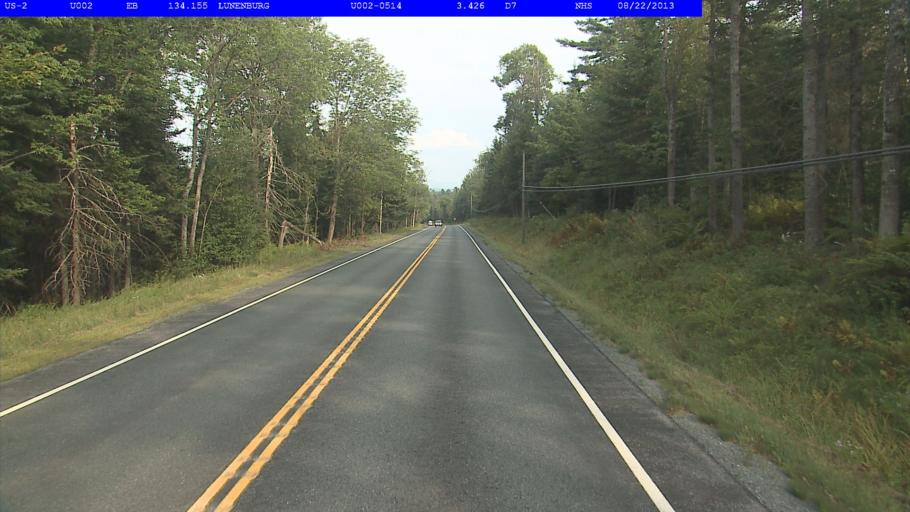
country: US
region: New Hampshire
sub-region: Coos County
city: Whitefield
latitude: 44.4630
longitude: -71.7072
